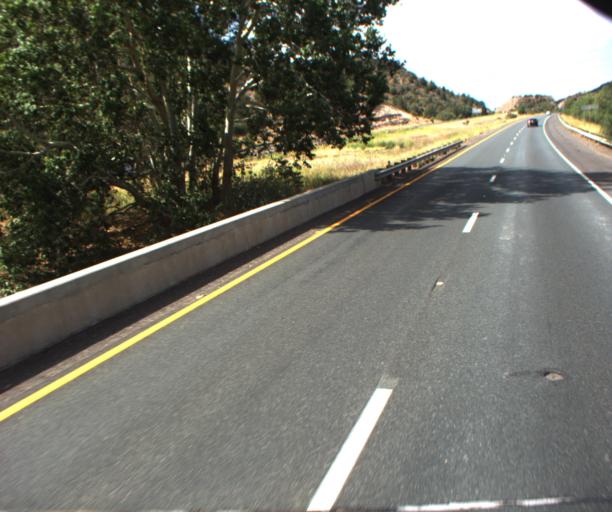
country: US
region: Arizona
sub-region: Yavapai County
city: Camp Verde
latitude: 34.5088
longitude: -111.9965
